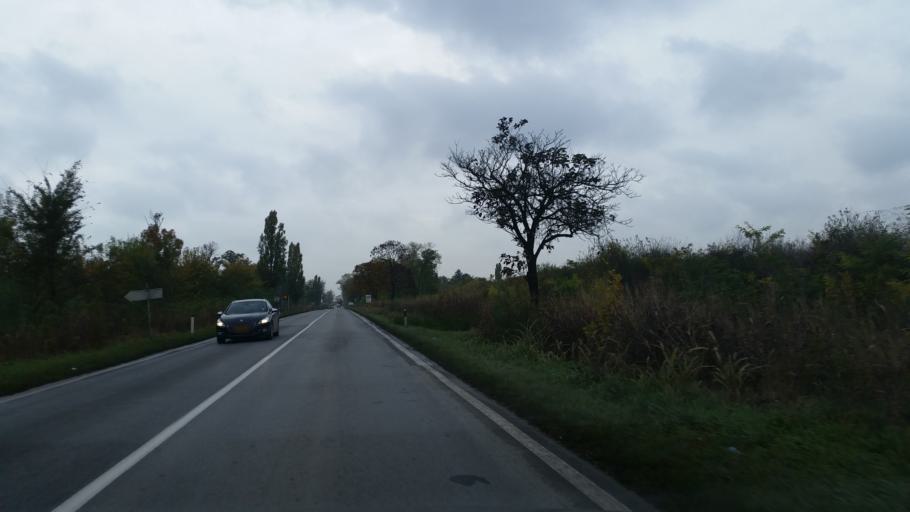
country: RS
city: Ecka
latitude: 45.3331
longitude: 20.4368
